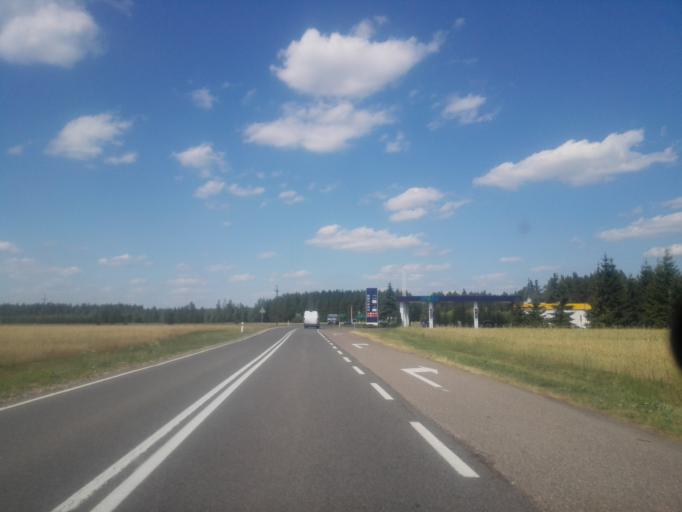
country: PL
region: Podlasie
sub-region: Powiat sejnenski
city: Sejny
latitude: 53.9815
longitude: 23.2940
